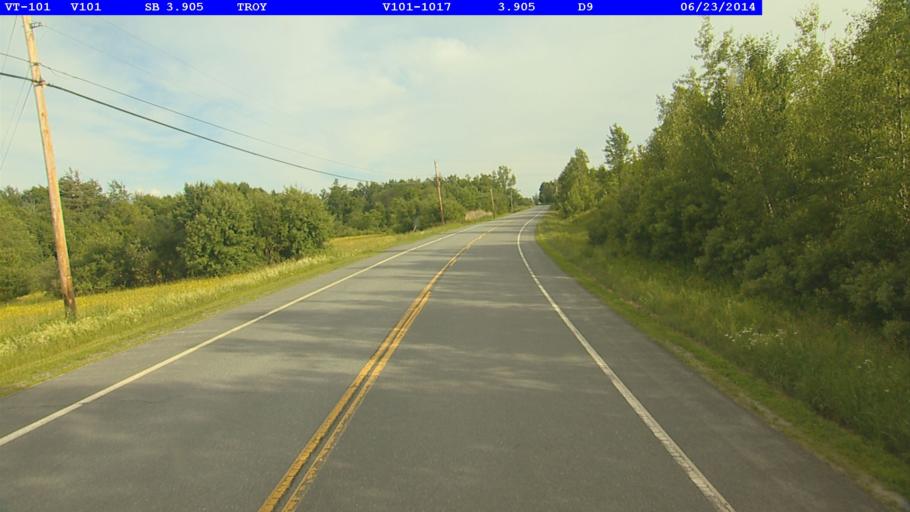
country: US
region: Vermont
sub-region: Orleans County
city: Newport
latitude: 44.9586
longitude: -72.4125
